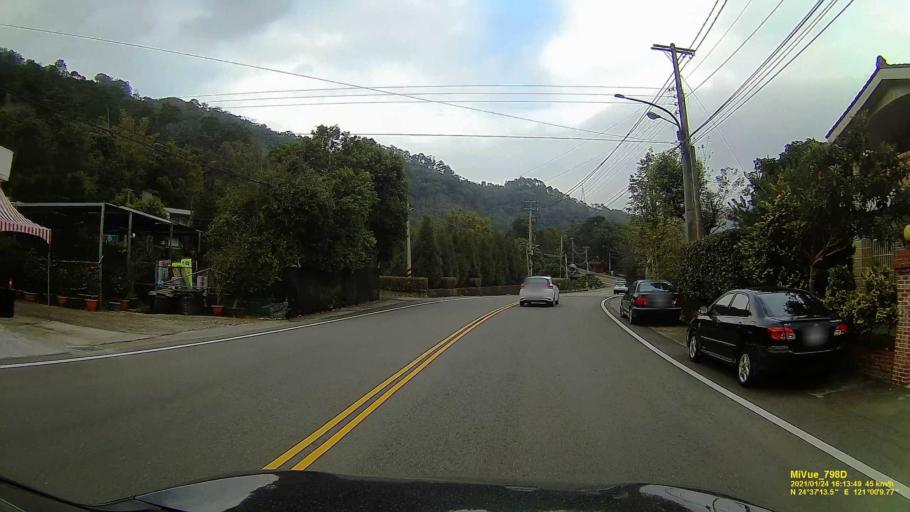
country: TW
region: Taiwan
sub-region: Hsinchu
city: Hsinchu
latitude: 24.6199
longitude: 121.0033
